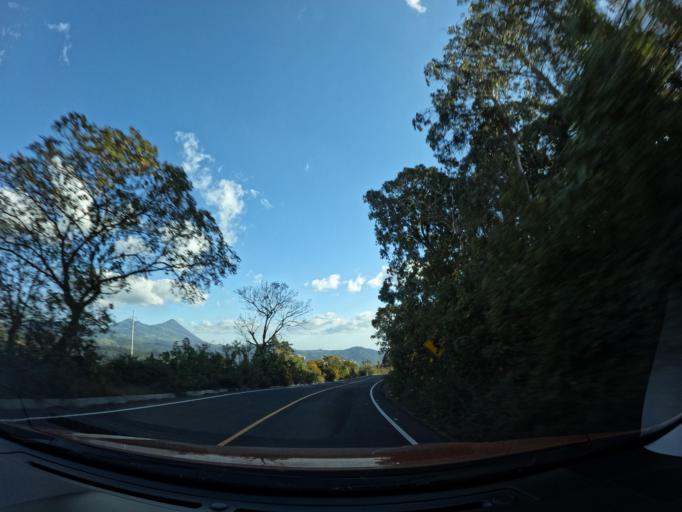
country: GT
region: Escuintla
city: Palin
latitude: 14.4506
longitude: -90.6927
